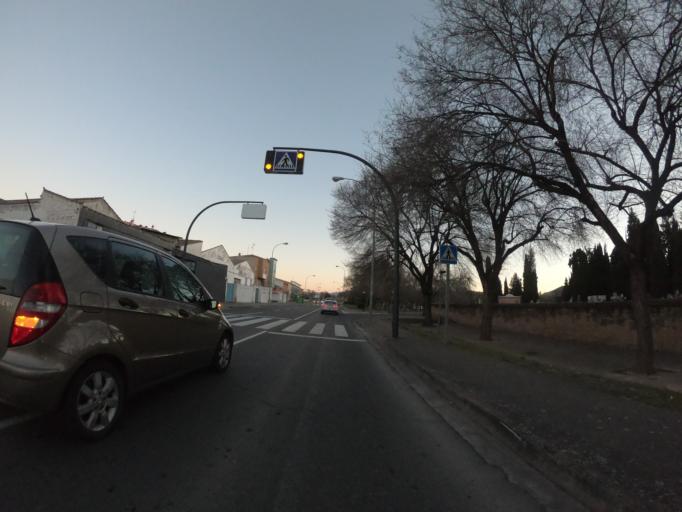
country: ES
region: La Rioja
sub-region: Provincia de La Rioja
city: Logrono
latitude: 42.4737
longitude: -2.4447
